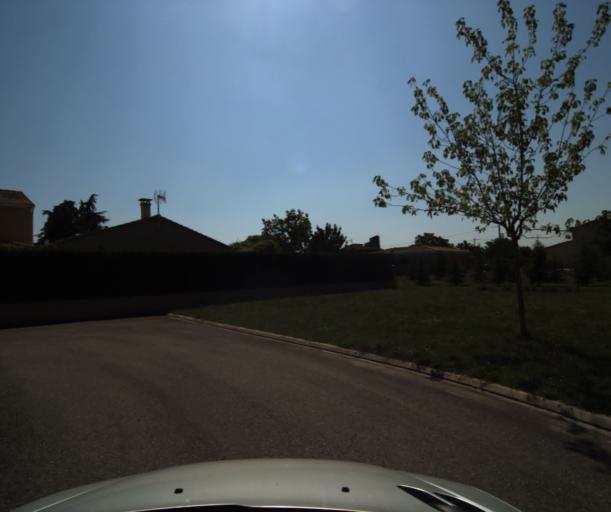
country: FR
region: Midi-Pyrenees
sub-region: Departement de la Haute-Garonne
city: Labarthe-sur-Leze
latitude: 43.4712
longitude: 1.3815
